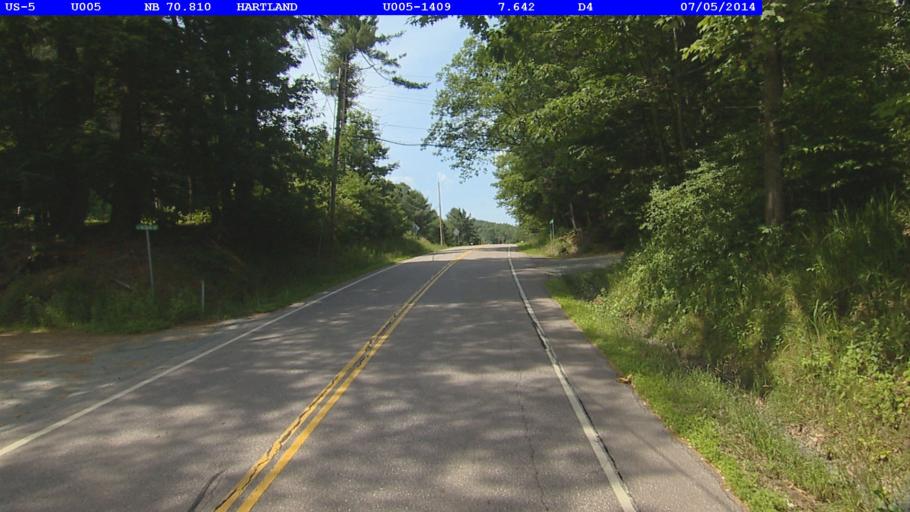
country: US
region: Vermont
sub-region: Windsor County
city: White River Junction
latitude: 43.6104
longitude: -72.3539
